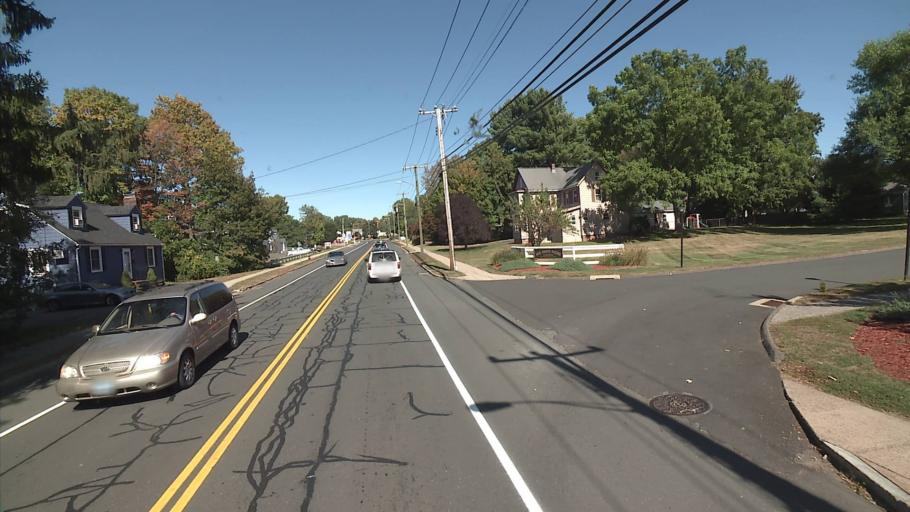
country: US
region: Connecticut
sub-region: Hartford County
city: Manchester
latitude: 41.8007
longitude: -72.5192
